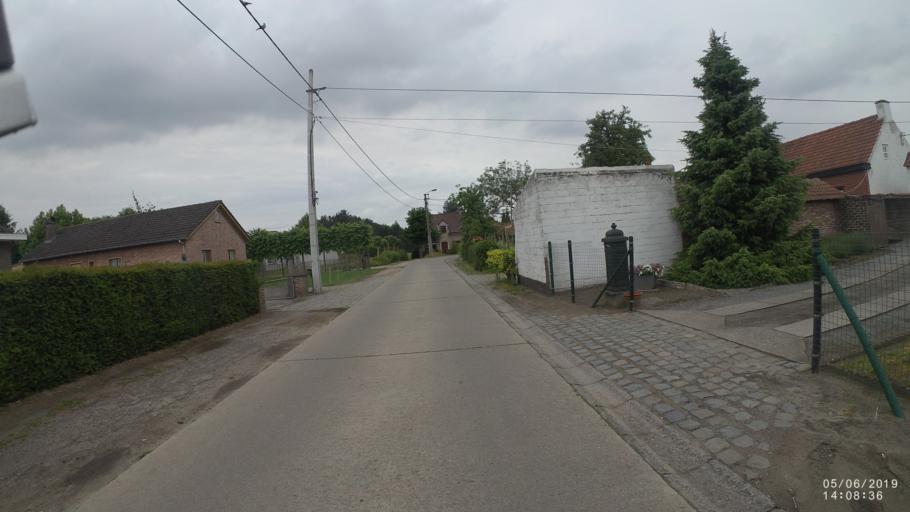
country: BE
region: Flanders
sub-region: Provincie Oost-Vlaanderen
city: Wachtebeke
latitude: 51.1897
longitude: 3.8554
